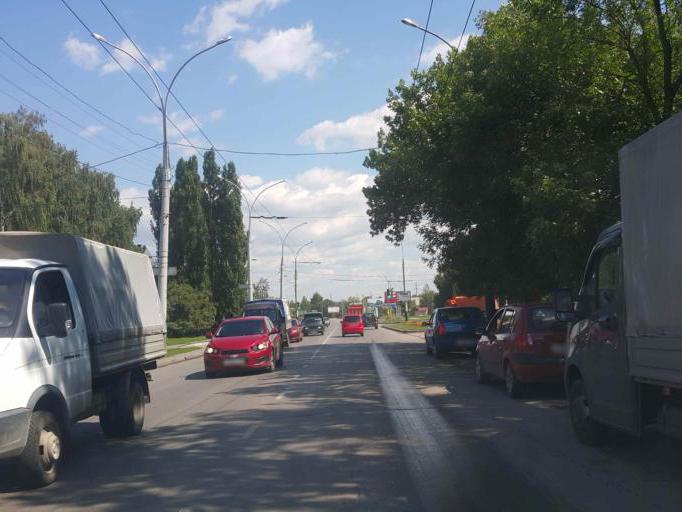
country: RU
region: Tambov
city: Donskoye
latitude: 52.7566
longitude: 41.4723
